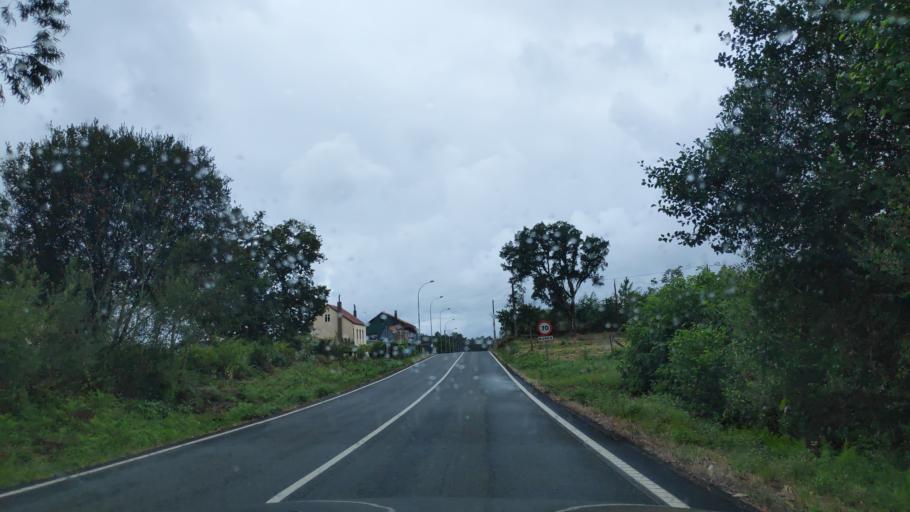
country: ES
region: Galicia
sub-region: Provincia de Pontevedra
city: Catoira
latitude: 42.6938
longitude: -8.7650
